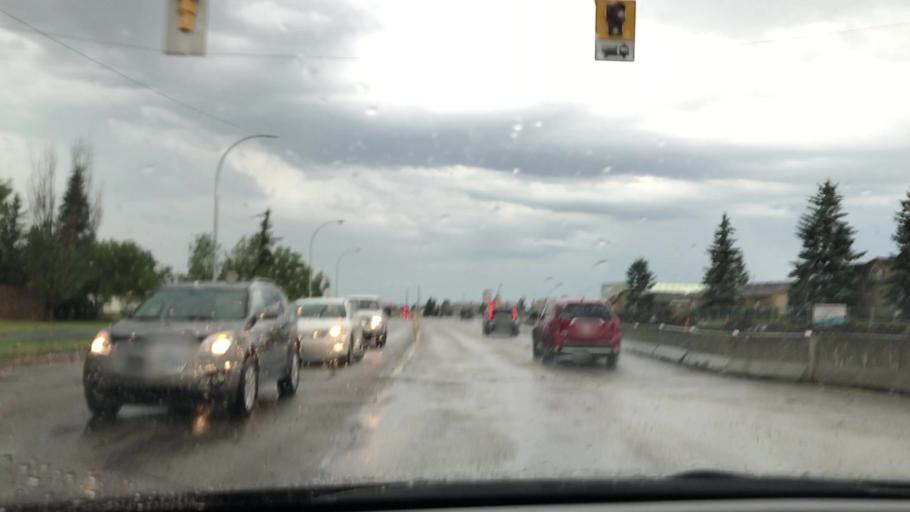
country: CA
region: Alberta
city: Edmonton
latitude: 53.4596
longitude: -113.4343
